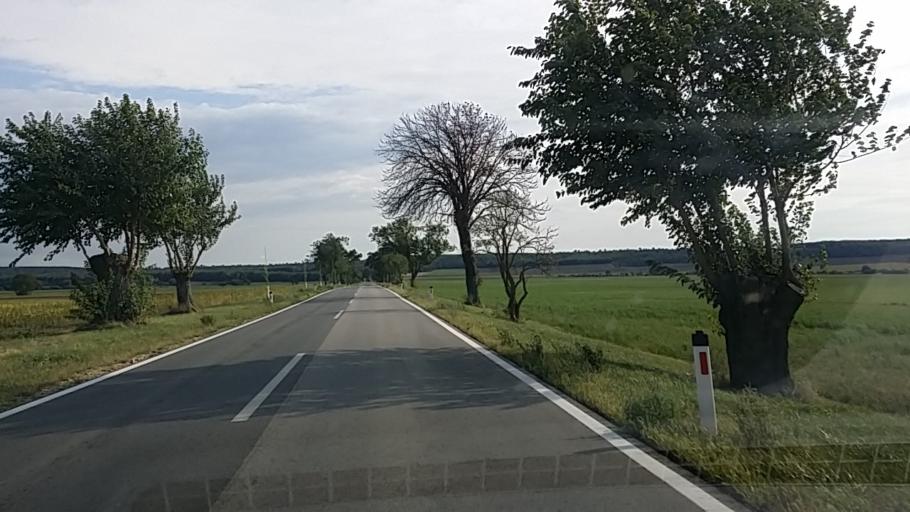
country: AT
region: Burgenland
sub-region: Eisenstadt-Umgebung
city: Sankt Margarethen im Burgenland
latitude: 47.7863
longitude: 16.6172
